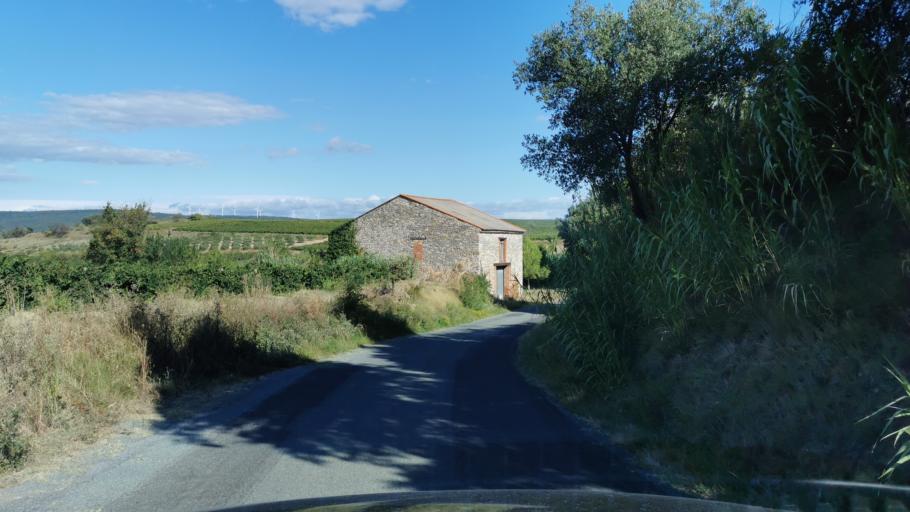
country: FR
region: Languedoc-Roussillon
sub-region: Departement de l'Aude
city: Ginestas
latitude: 43.2621
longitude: 2.8442
